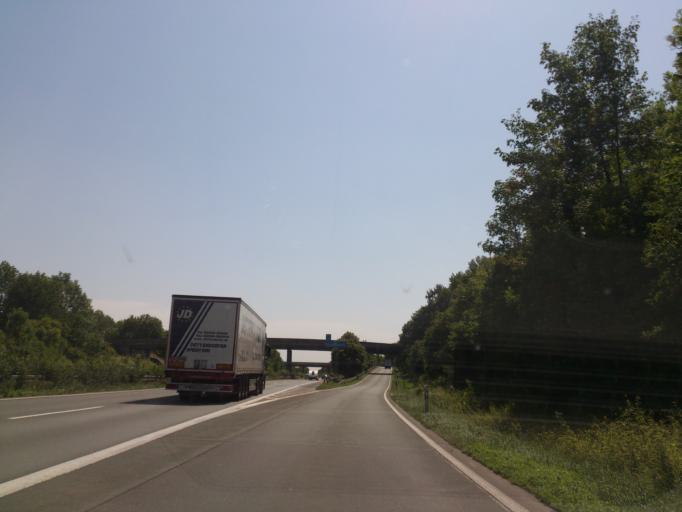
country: DE
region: North Rhine-Westphalia
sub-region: Regierungsbezirk Detmold
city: Paderborn
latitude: 51.6849
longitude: 8.7129
